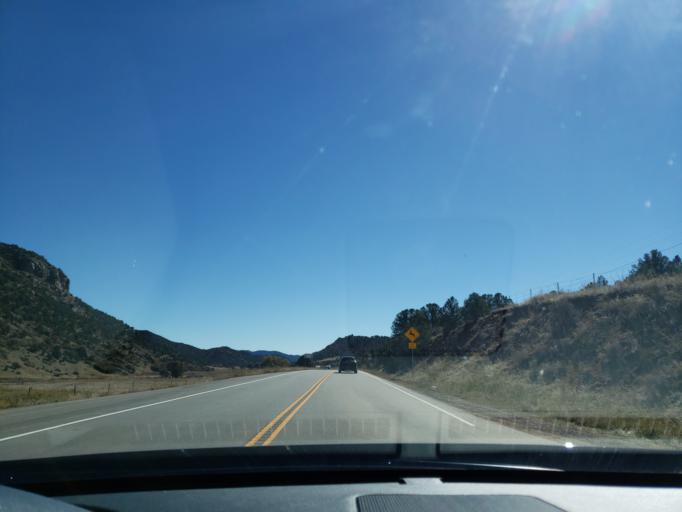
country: US
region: Colorado
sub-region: Fremont County
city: Canon City
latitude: 38.6116
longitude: -105.4414
